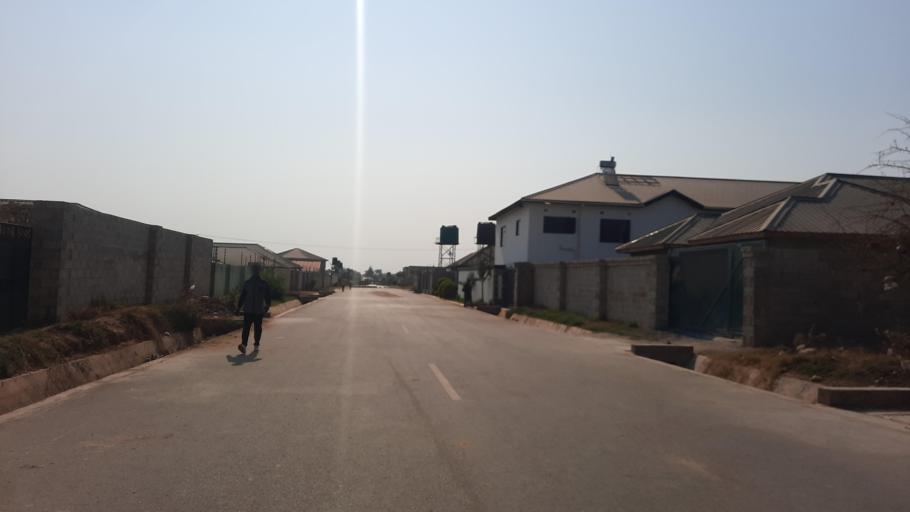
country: ZM
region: Lusaka
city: Lusaka
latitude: -15.3922
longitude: 28.3858
